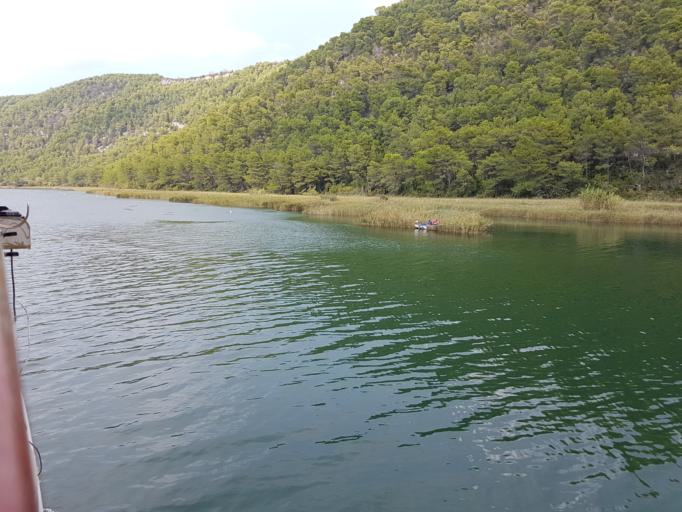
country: HR
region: Sibensko-Kniniska
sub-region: Grad Sibenik
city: Sibenik
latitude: 43.8148
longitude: 15.9515
